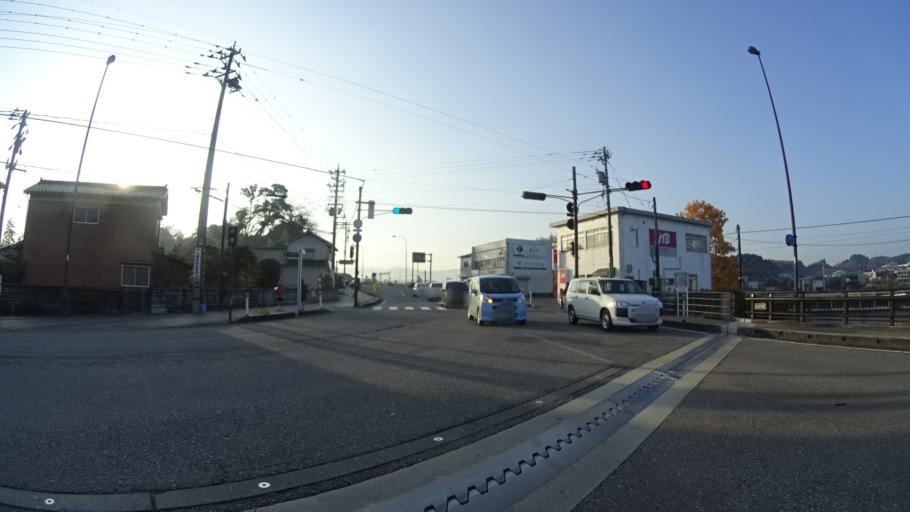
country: JP
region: Ishikawa
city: Nanao
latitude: 37.0480
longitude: 136.9574
